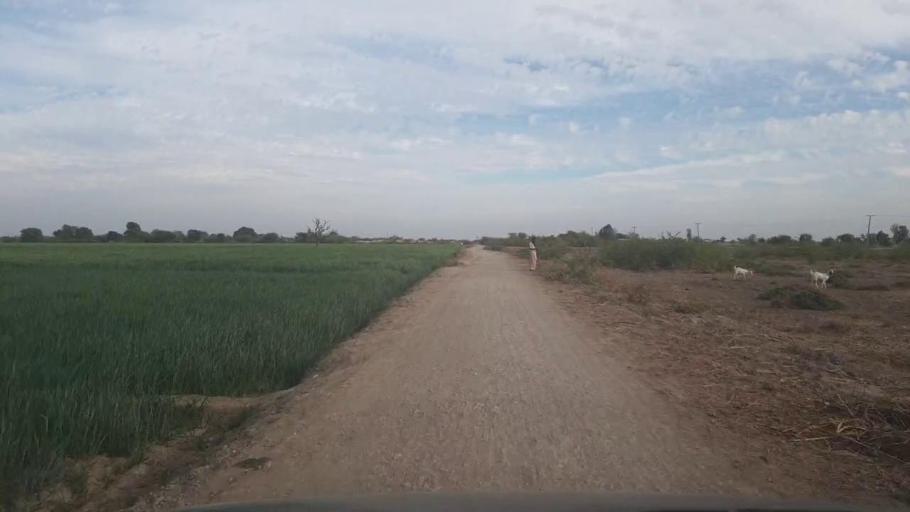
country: PK
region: Sindh
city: Samaro
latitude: 25.3311
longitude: 69.2575
